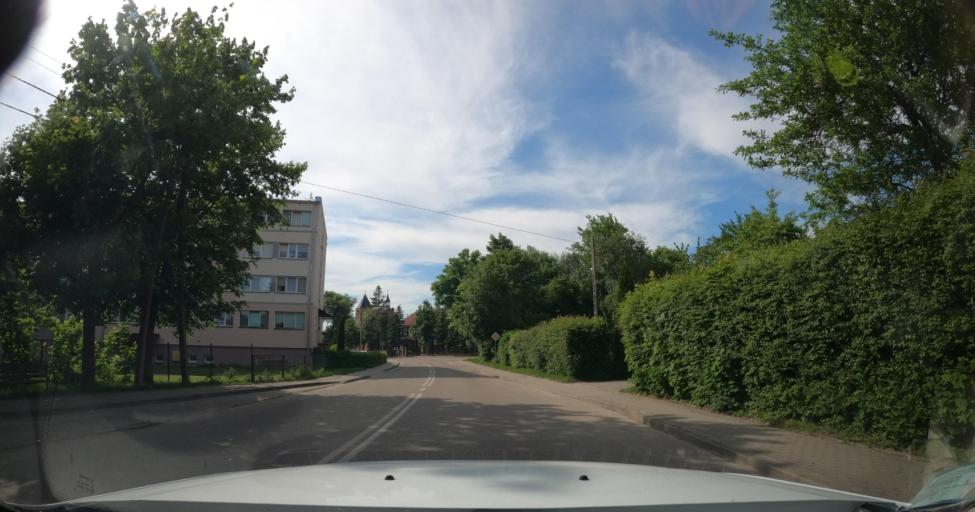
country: PL
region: Warmian-Masurian Voivodeship
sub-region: Powiat ostrodzki
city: Milakowo
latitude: 54.0091
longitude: 20.0773
